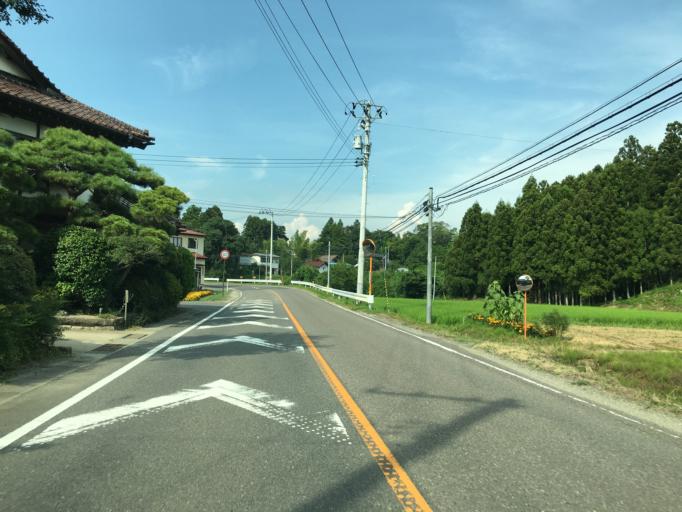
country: JP
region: Fukushima
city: Koriyama
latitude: 37.3507
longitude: 140.4150
